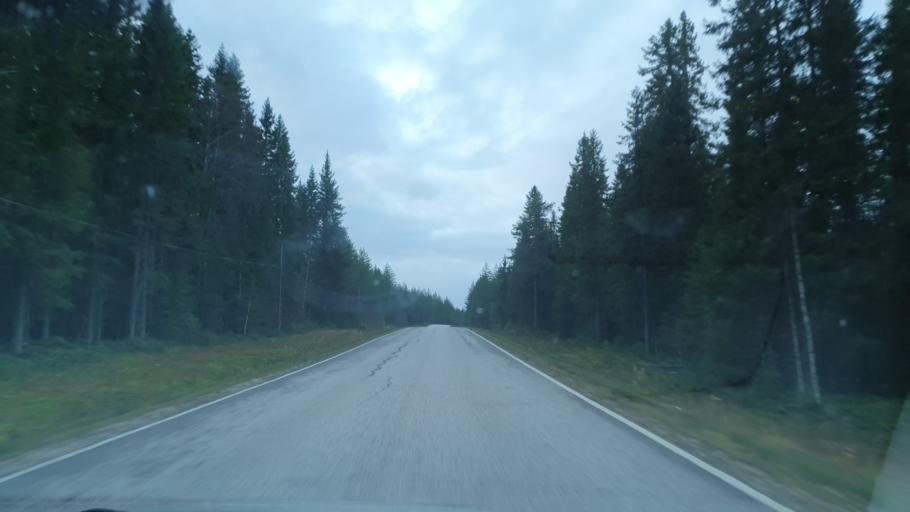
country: FI
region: Kainuu
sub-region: Kajaani
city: Ristijaervi
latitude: 64.4290
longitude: 28.3754
